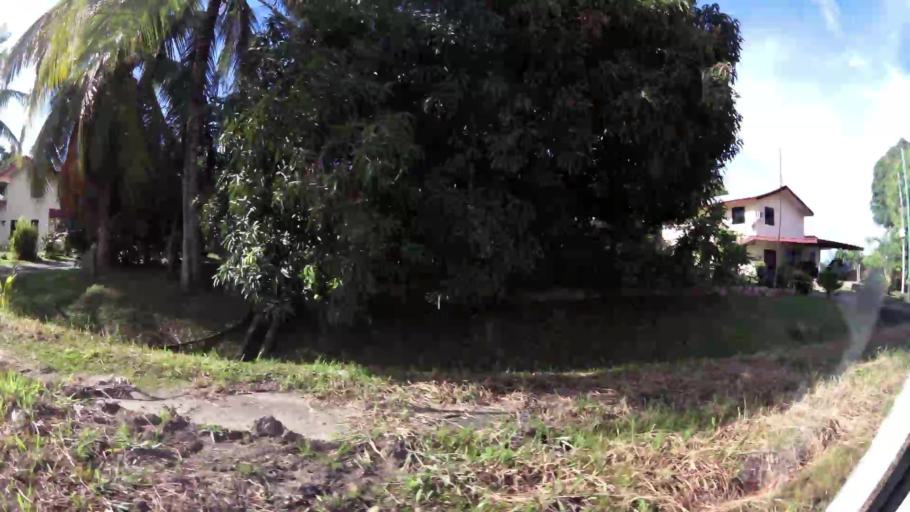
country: BN
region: Brunei and Muara
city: Bandar Seri Begawan
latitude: 4.9779
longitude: 114.9662
